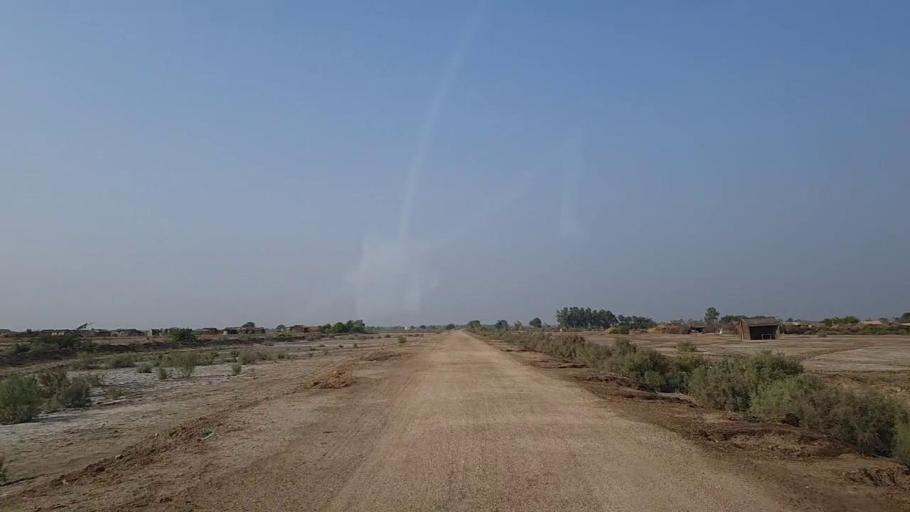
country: PK
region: Sindh
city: Mirpur Sakro
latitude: 24.6294
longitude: 67.7680
